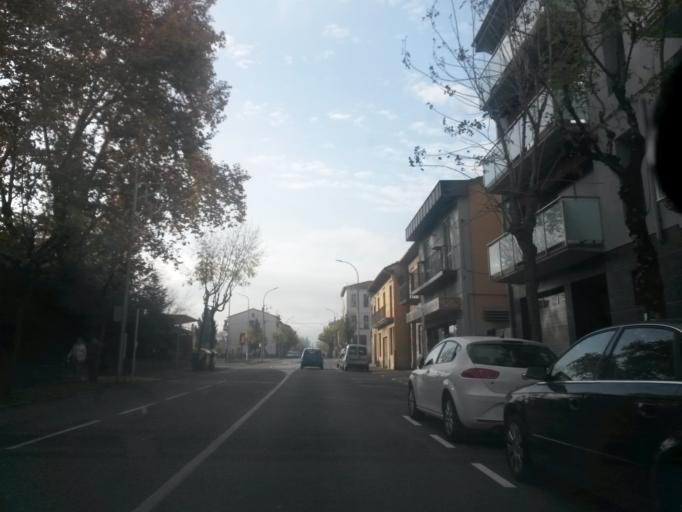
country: ES
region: Catalonia
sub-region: Provincia de Girona
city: Olot
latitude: 42.1726
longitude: 2.4789
